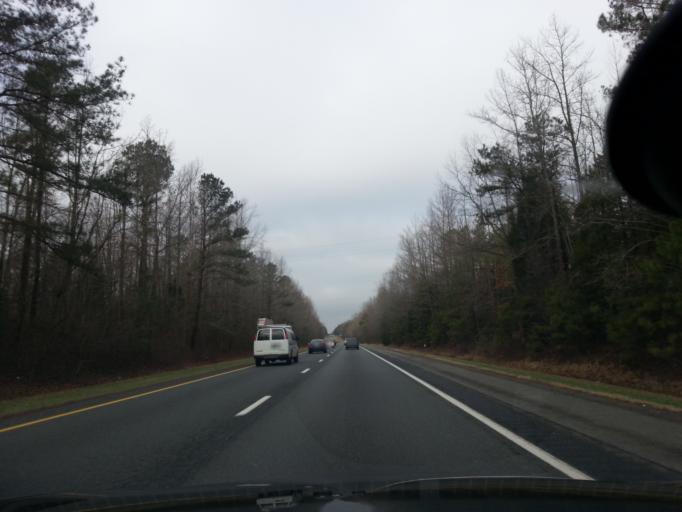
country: US
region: Virginia
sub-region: New Kent County
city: New Kent
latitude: 37.5084
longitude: -77.1094
